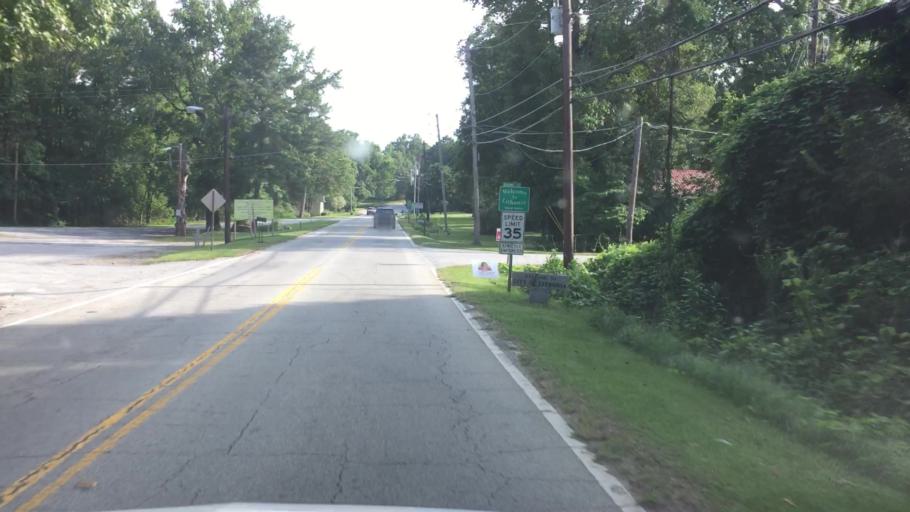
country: US
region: Georgia
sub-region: DeKalb County
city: Lithonia
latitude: 33.7193
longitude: -84.1015
